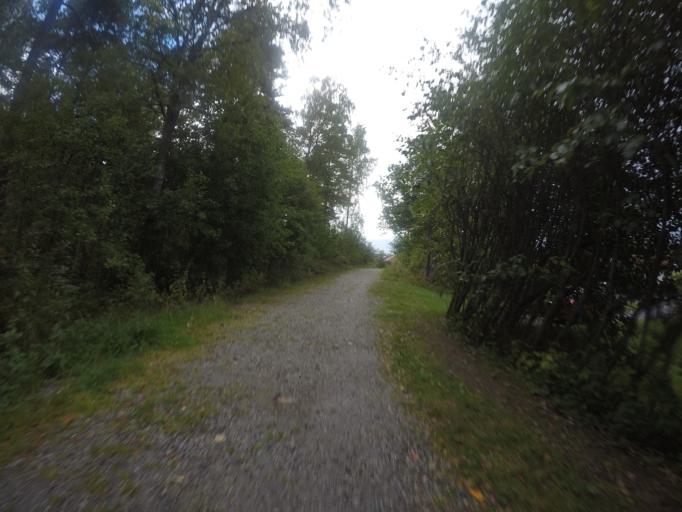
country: SE
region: Vaestmanland
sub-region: Vasteras
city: Vasteras
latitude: 59.6533
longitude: 16.5313
